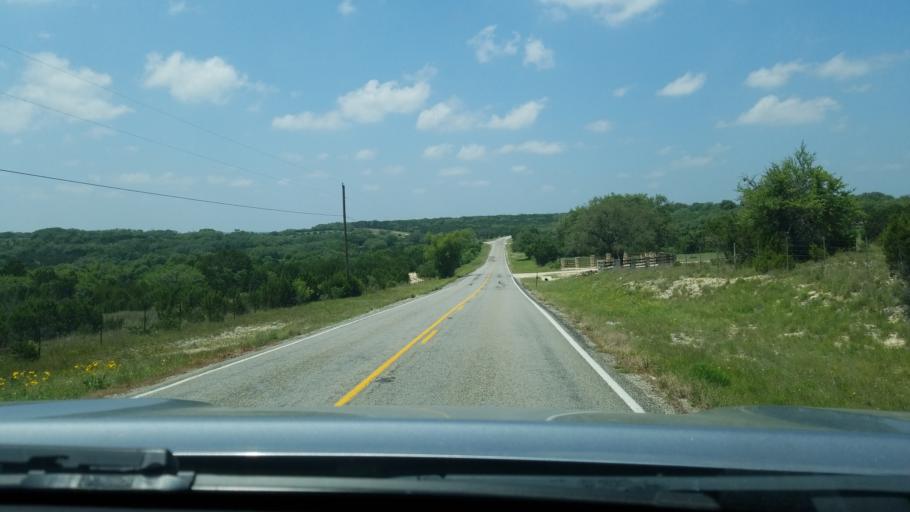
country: US
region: Texas
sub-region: Hays County
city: Woodcreek
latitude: 30.0645
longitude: -98.2144
